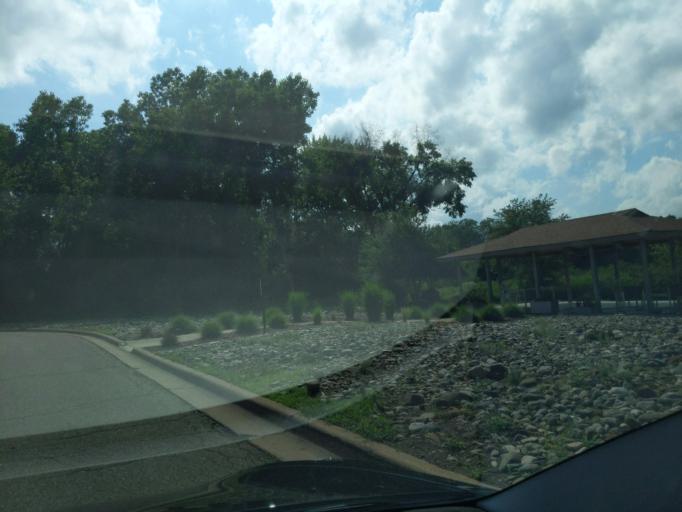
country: US
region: Michigan
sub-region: Jackson County
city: Jackson
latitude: 42.2263
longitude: -84.3699
